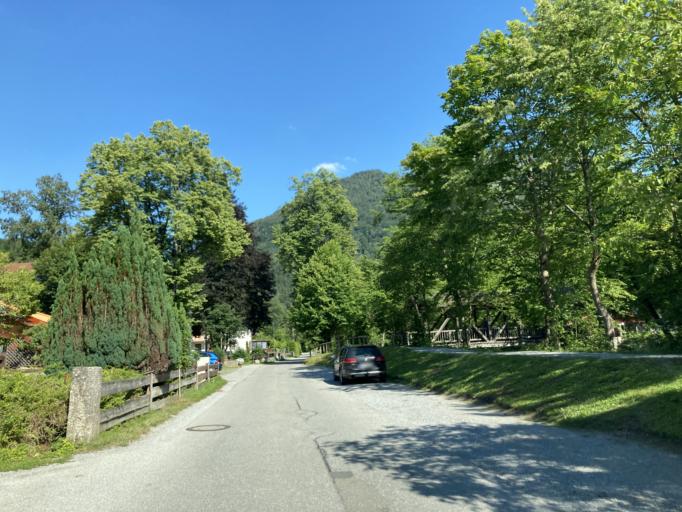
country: DE
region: Bavaria
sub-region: Upper Bavaria
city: Nussdorf am Inn
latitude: 47.7428
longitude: 12.1595
